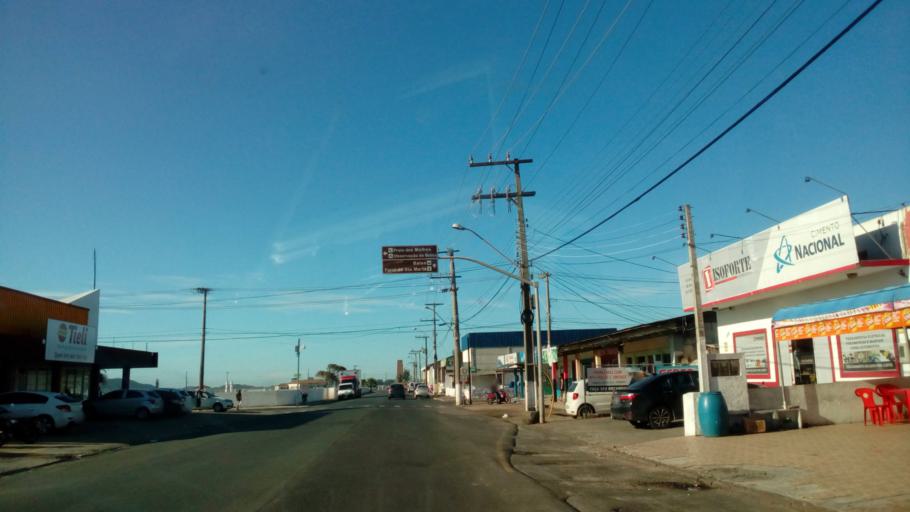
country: BR
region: Santa Catarina
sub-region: Laguna
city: Laguna
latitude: -28.4929
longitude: -48.7726
